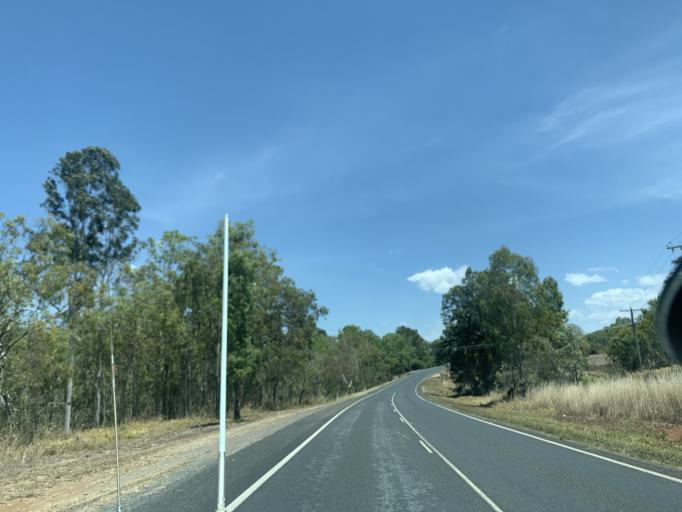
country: AU
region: Queensland
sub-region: Tablelands
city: Mareeba
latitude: -16.9569
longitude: 145.5397
